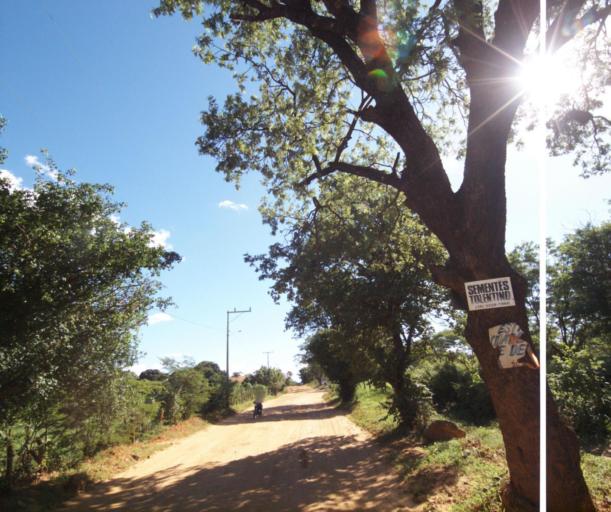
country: BR
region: Bahia
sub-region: Carinhanha
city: Carinhanha
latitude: -14.1912
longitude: -44.5457
